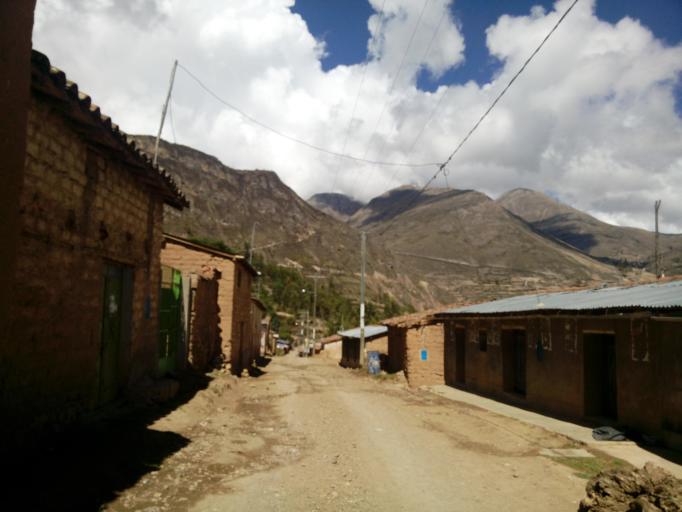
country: PE
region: Ayacucho
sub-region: Provincia de Victor Fajardo
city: Canaria
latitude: -13.8778
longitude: -73.9352
